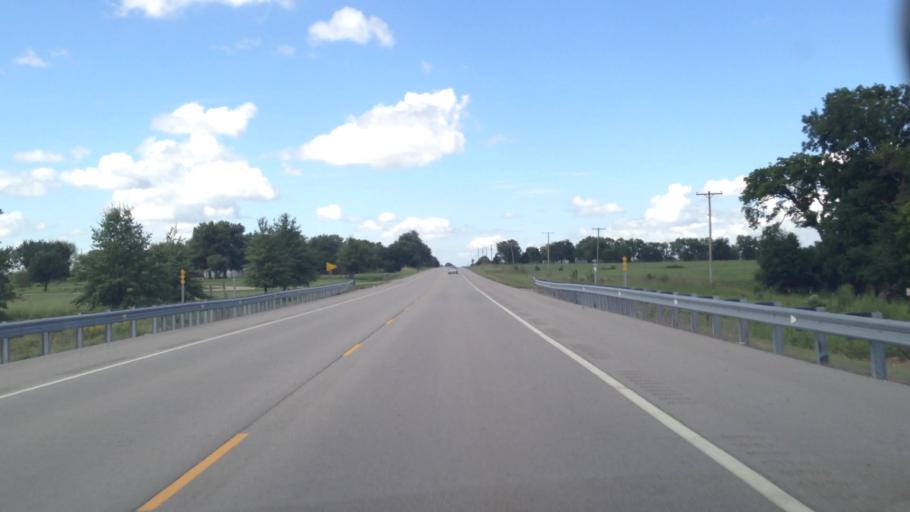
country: US
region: Kansas
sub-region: Labette County
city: Altamont
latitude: 37.2231
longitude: -95.2672
